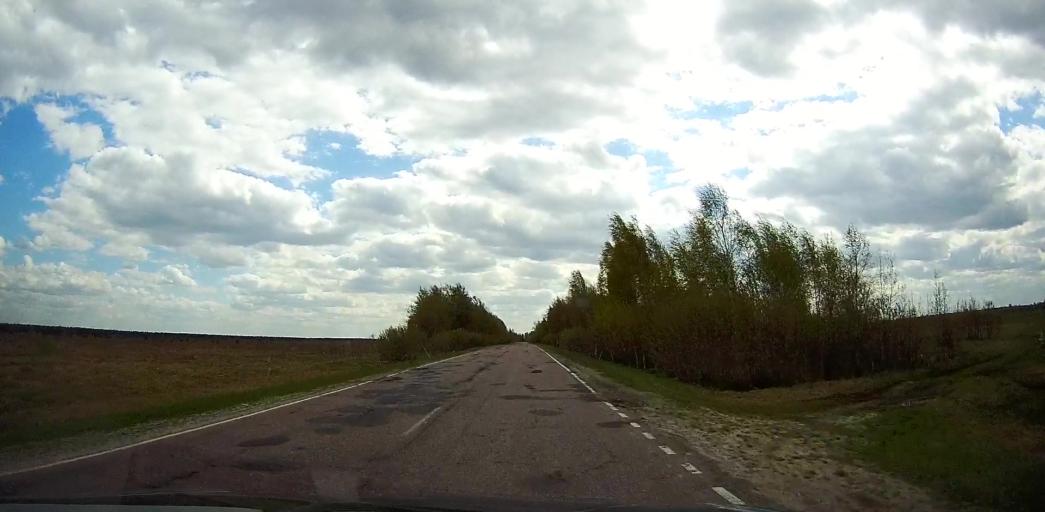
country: RU
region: Moskovskaya
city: Davydovo
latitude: 55.6383
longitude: 38.7479
